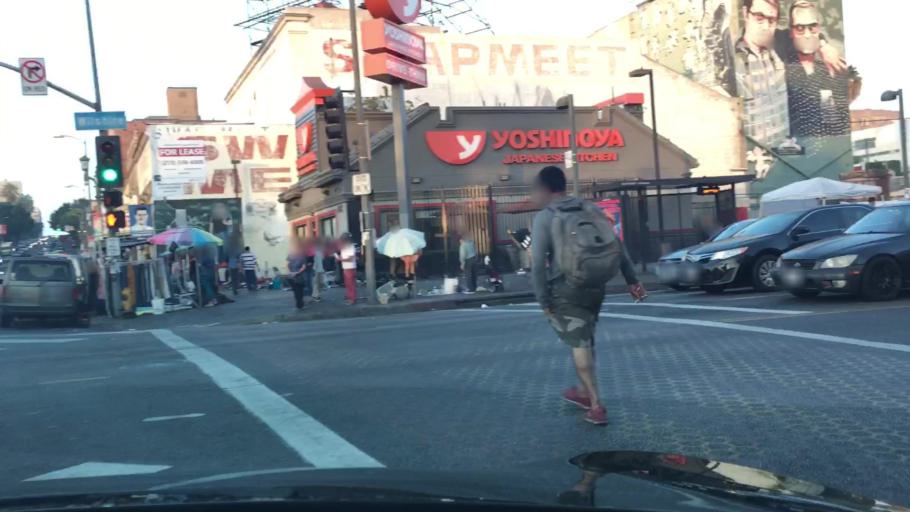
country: US
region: California
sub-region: Los Angeles County
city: Echo Park
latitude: 34.0578
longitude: -118.2759
